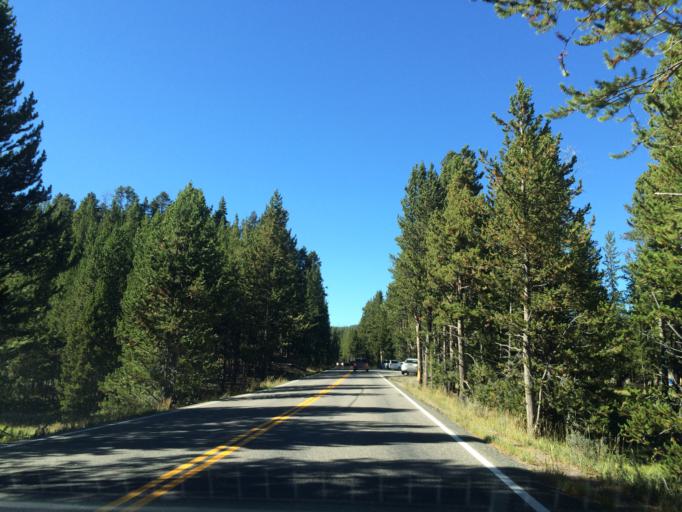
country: US
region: Montana
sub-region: Gallatin County
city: West Yellowstone
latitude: 44.6978
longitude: -110.5025
